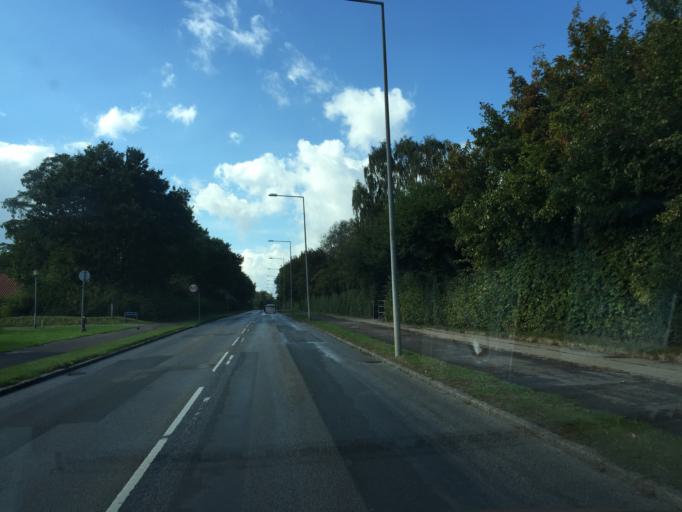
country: DK
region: South Denmark
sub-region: Sonderborg Kommune
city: Nordborg
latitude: 55.0549
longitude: 9.7560
